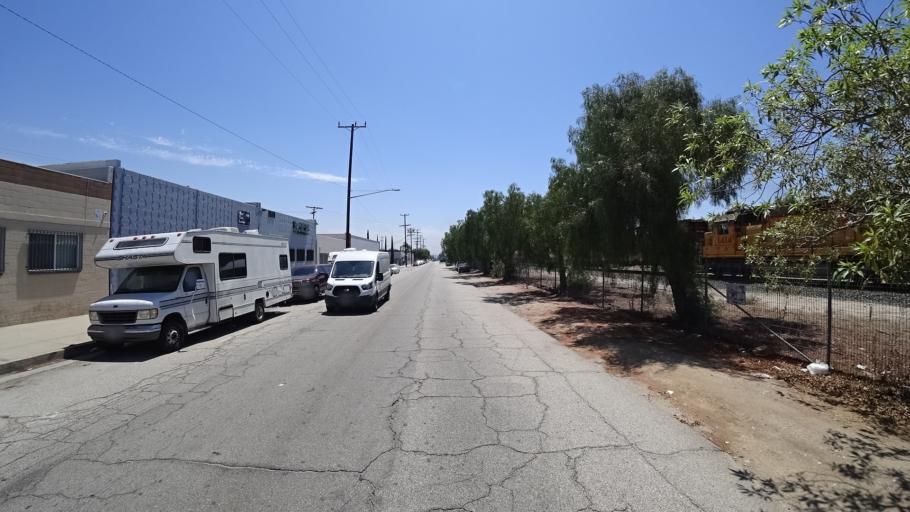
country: US
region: California
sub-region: Los Angeles County
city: North Hollywood
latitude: 34.2094
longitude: -118.3540
